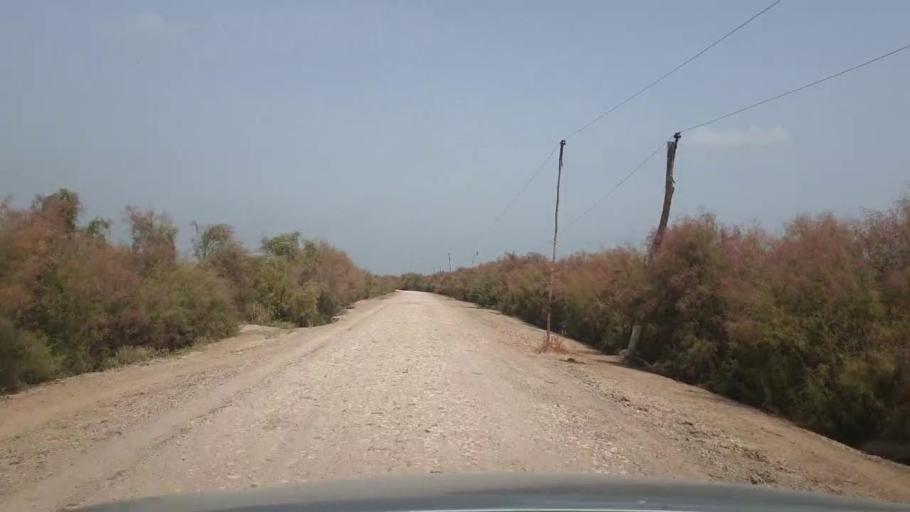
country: PK
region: Sindh
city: Garhi Yasin
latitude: 27.9552
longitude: 68.3652
